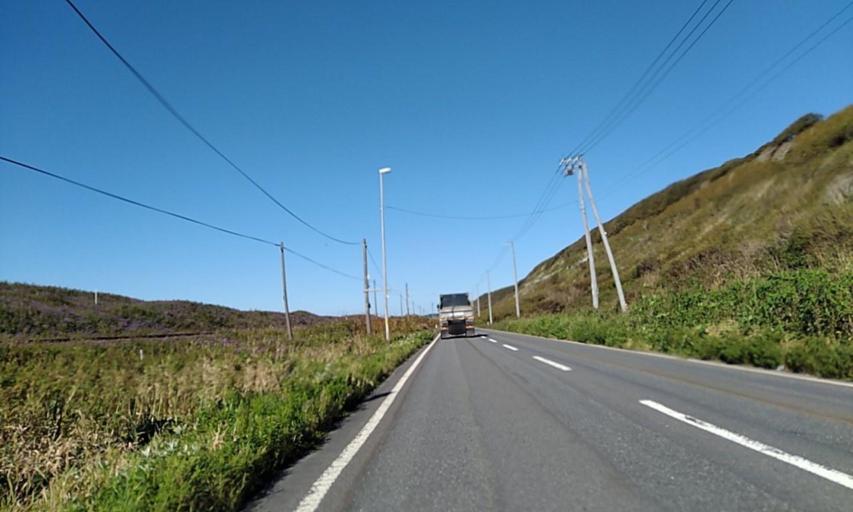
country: JP
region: Hokkaido
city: Shizunai-furukawacho
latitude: 42.4663
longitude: 142.1452
